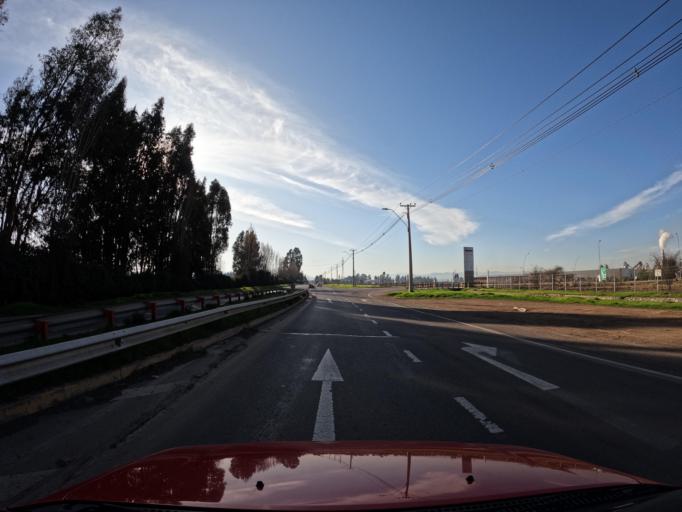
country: CL
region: Maule
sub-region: Provincia de Curico
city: Teno
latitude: -34.8657
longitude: -71.0911
